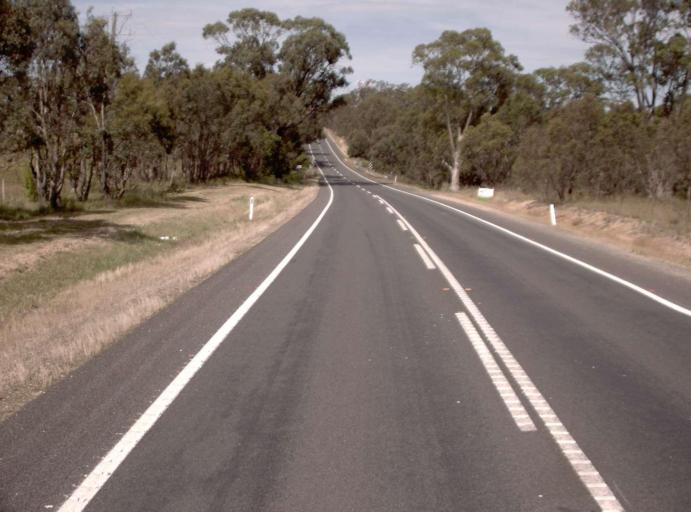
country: AU
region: Victoria
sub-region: East Gippsland
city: Bairnsdale
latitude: -37.9008
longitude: 147.3545
